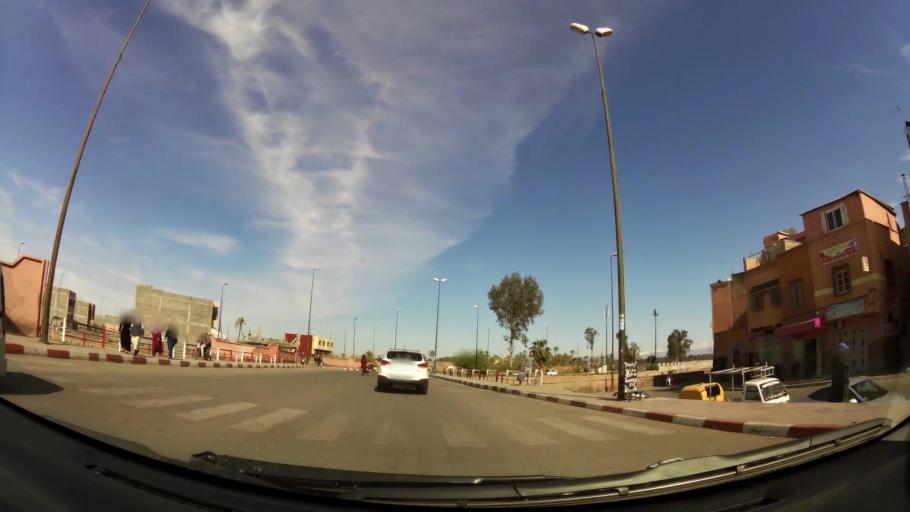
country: MA
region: Marrakech-Tensift-Al Haouz
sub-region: Marrakech
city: Marrakesh
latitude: 31.6224
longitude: -7.9696
